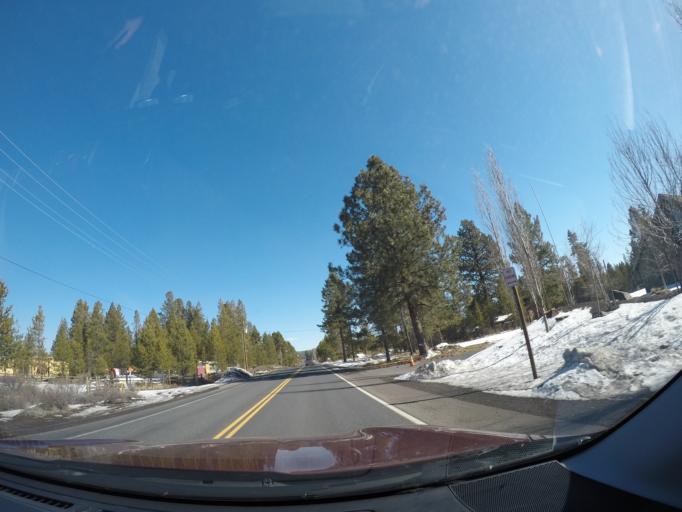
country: US
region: Oregon
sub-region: Deschutes County
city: Sunriver
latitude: 43.8630
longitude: -121.4617
